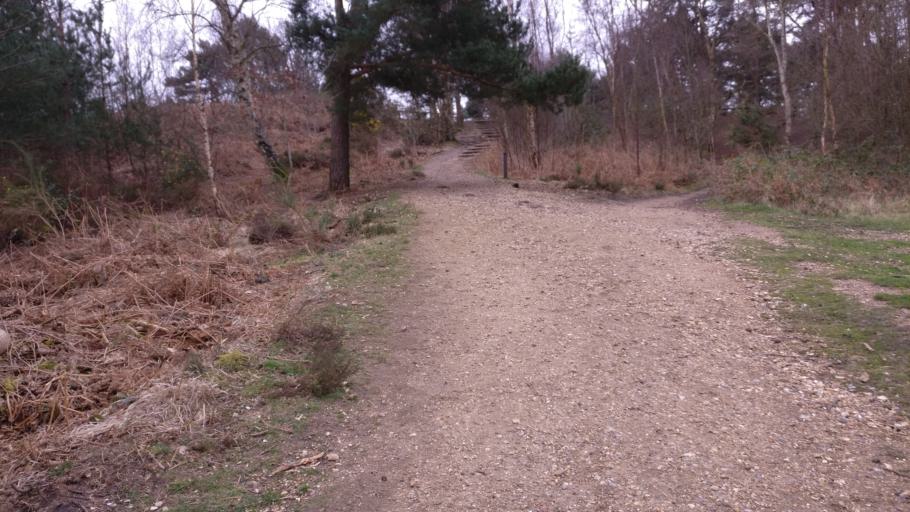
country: GB
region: England
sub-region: Surrey
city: Bagshot
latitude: 51.3469
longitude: -0.6920
